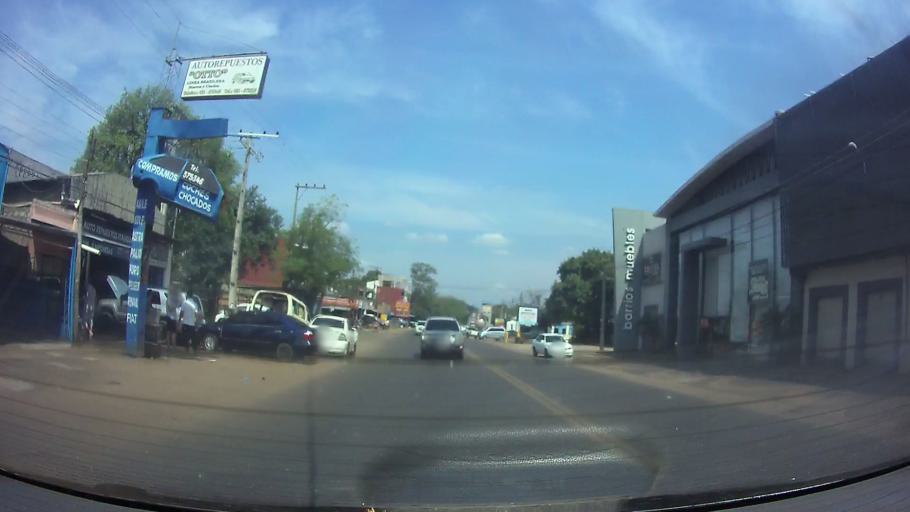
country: PY
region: Central
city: San Lorenzo
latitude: -25.3547
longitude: -57.4891
